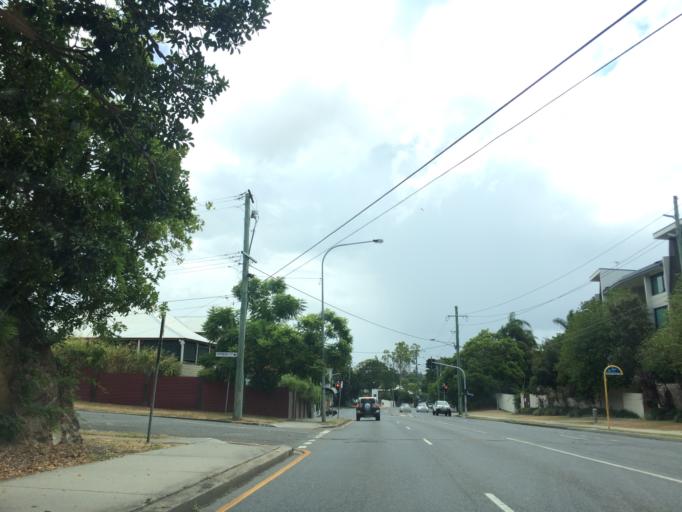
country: AU
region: Queensland
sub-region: Brisbane
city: Balmoral
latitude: -27.4744
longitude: 153.0555
